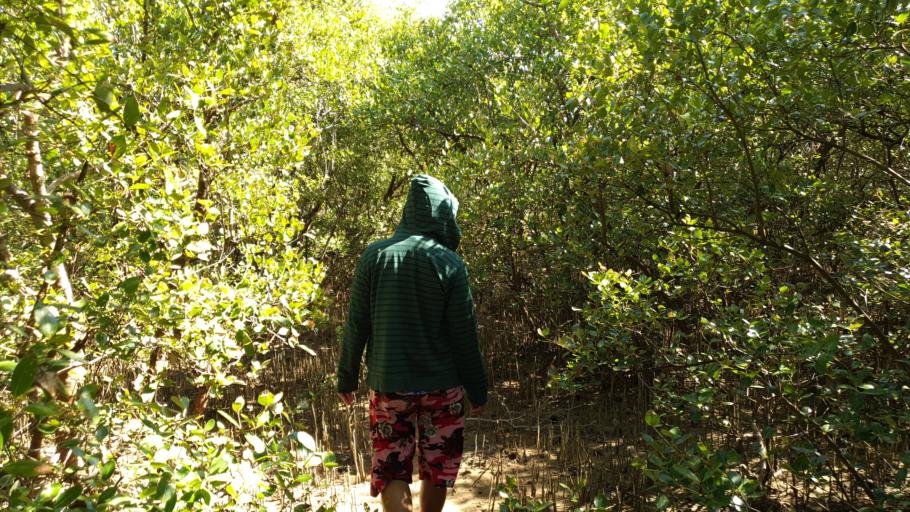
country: PH
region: Ilocos
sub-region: Province of La Union
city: Payocpoc Sur
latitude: 16.5040
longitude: 120.3087
